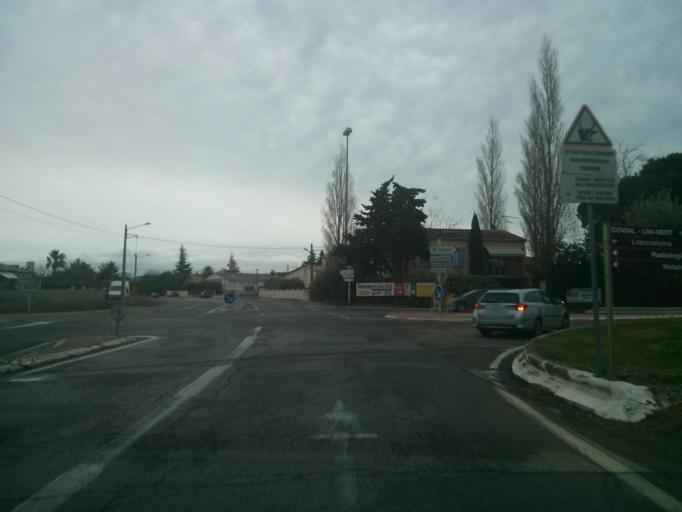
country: FR
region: Languedoc-Roussillon
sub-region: Departement du Gard
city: Saint-Gilles
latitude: 43.6732
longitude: 4.4212
